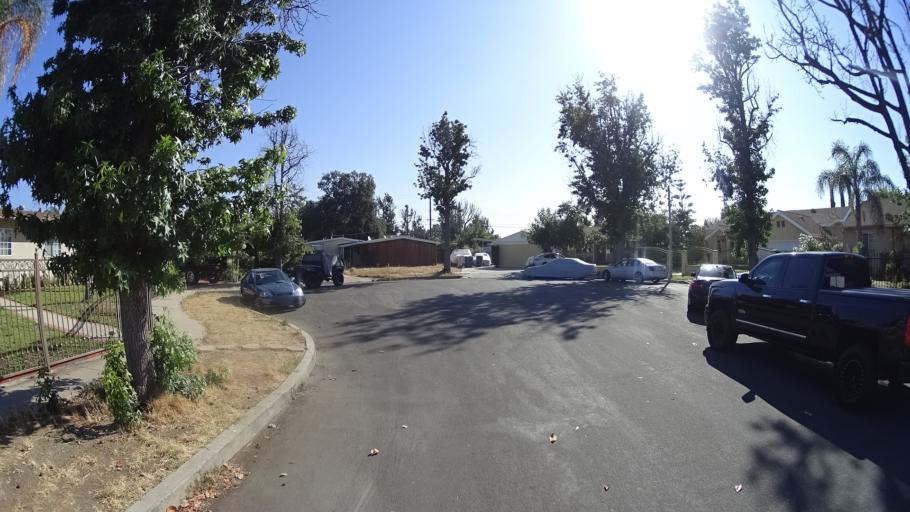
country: US
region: California
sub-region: Los Angeles County
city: Van Nuys
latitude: 34.2248
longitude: -118.4296
